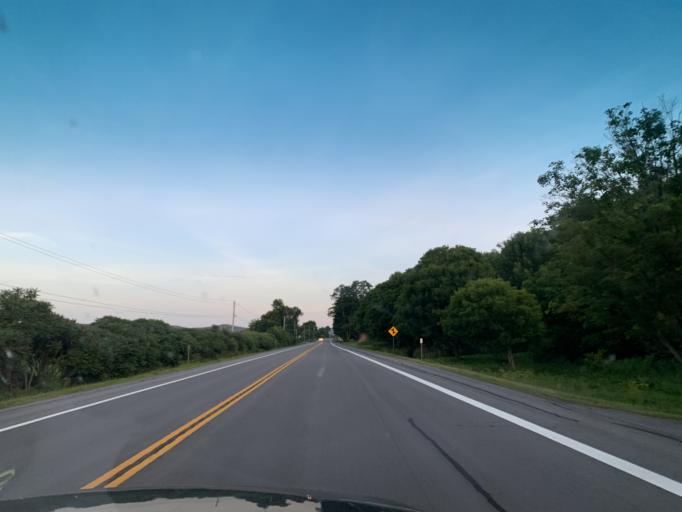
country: US
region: New York
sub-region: Oneida County
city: Chadwicks
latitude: 42.9351
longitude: -75.2506
